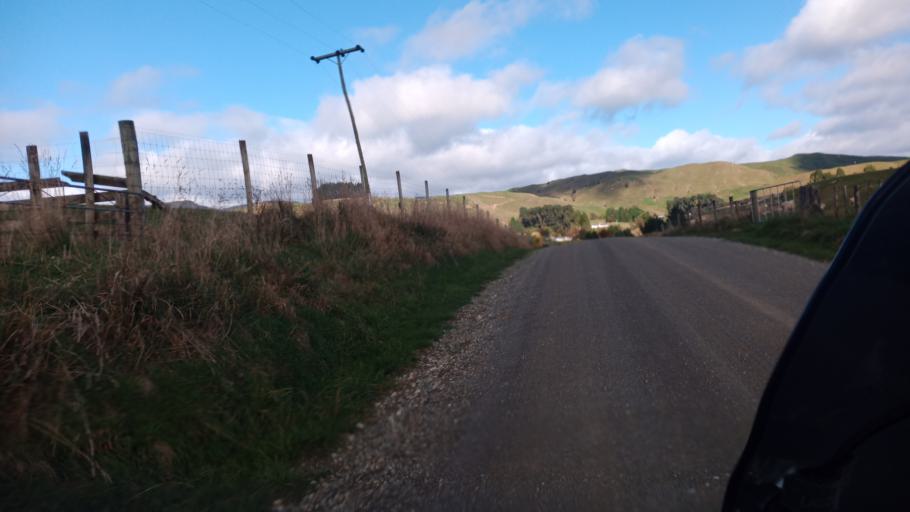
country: NZ
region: Bay of Plenty
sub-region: Opotiki District
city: Opotiki
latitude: -38.4576
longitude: 177.3912
